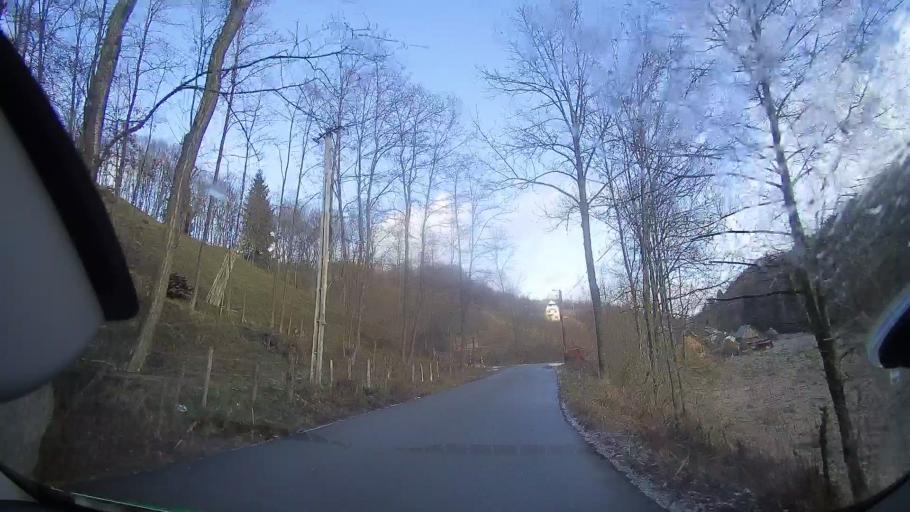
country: RO
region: Alba
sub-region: Comuna Sohodol
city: Sohodol
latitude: 46.3420
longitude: 23.0147
